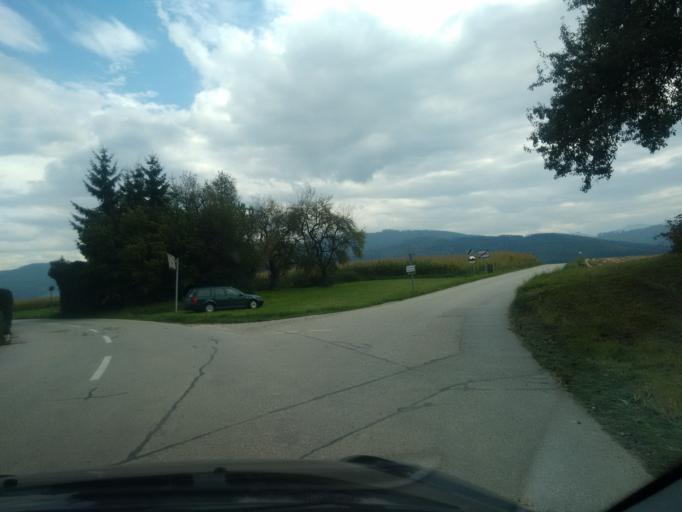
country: AT
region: Upper Austria
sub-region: Politischer Bezirk Vocklabruck
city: Lenzing
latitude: 47.9597
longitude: 13.6349
